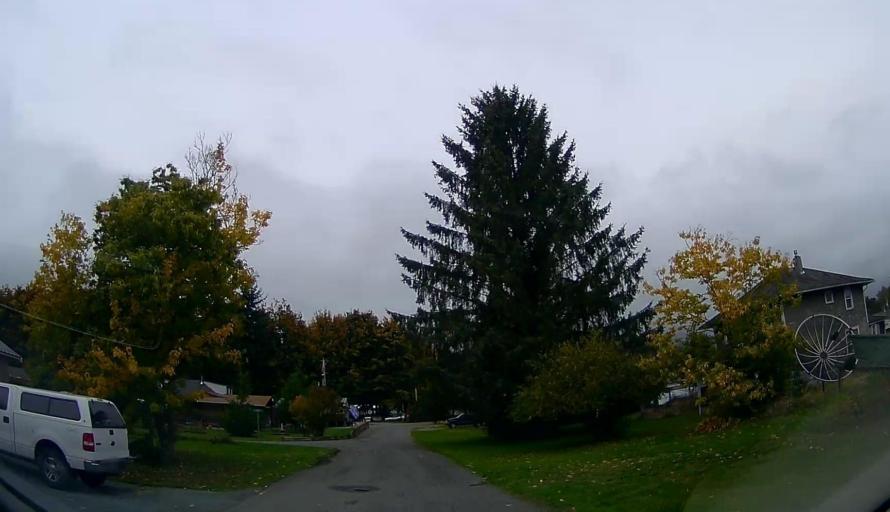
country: US
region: Washington
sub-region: Skagit County
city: Sedro-Woolley
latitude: 48.5252
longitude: -122.0611
